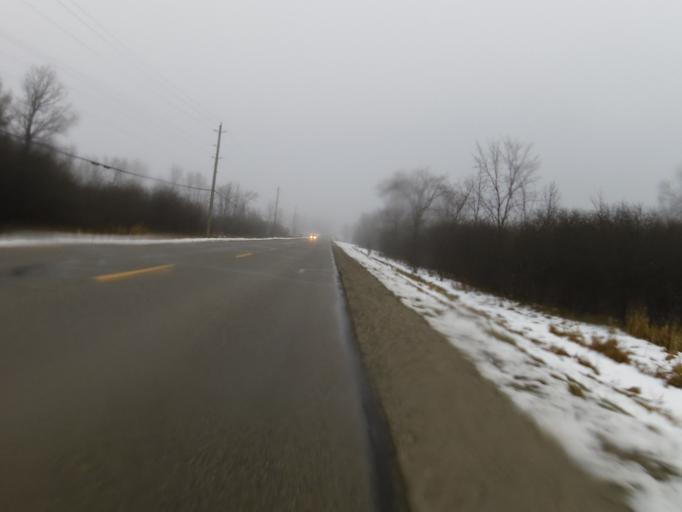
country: CA
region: Ontario
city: Perth
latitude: 44.8749
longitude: -76.3205
